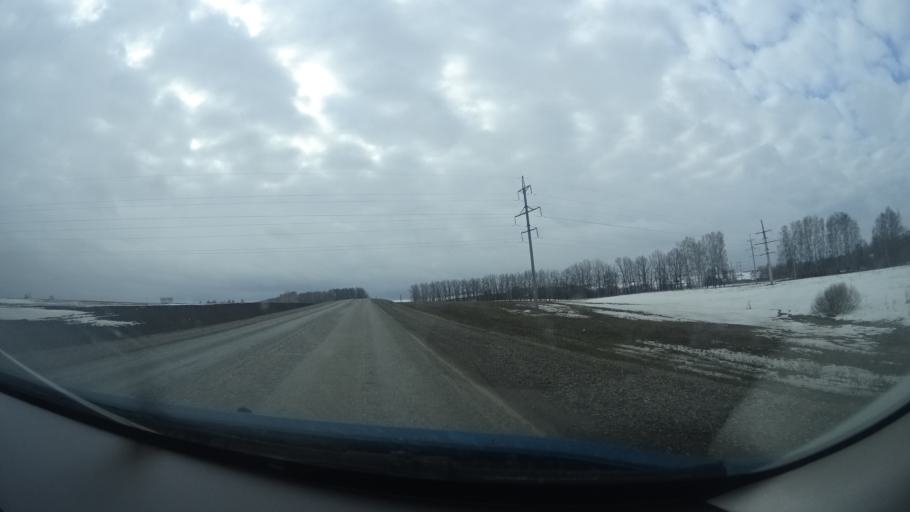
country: RU
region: Bashkortostan
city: Birsk
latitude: 55.4102
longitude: 55.5870
